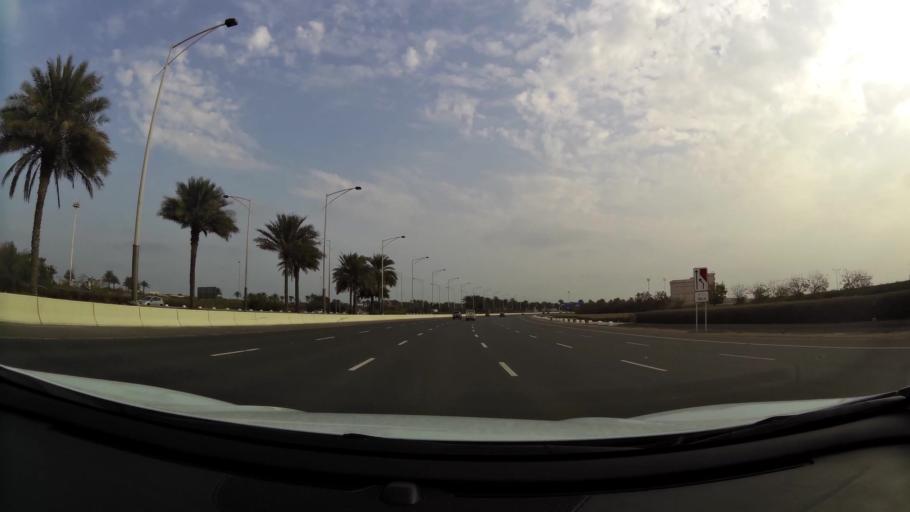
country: AE
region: Abu Dhabi
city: Abu Dhabi
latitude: 24.5385
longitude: 54.4371
